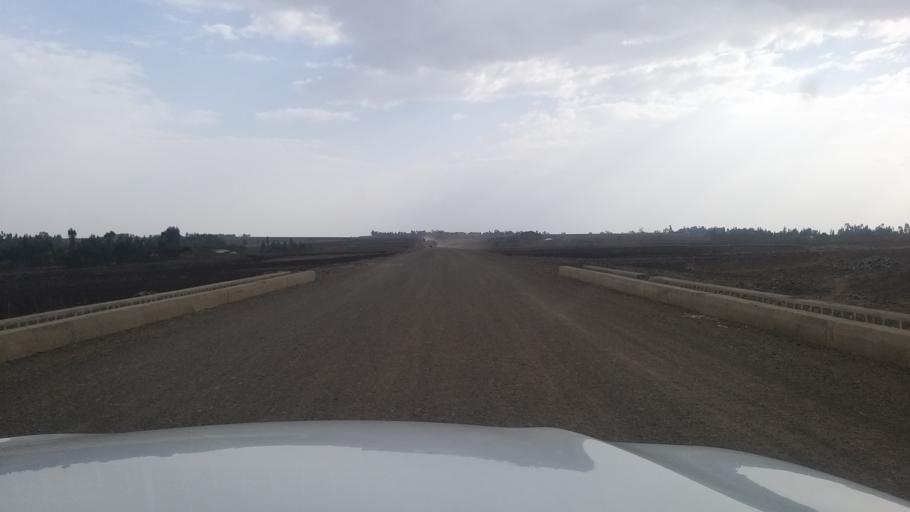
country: ET
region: Amhara
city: Were Ilu
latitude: 10.4466
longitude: 39.1989
